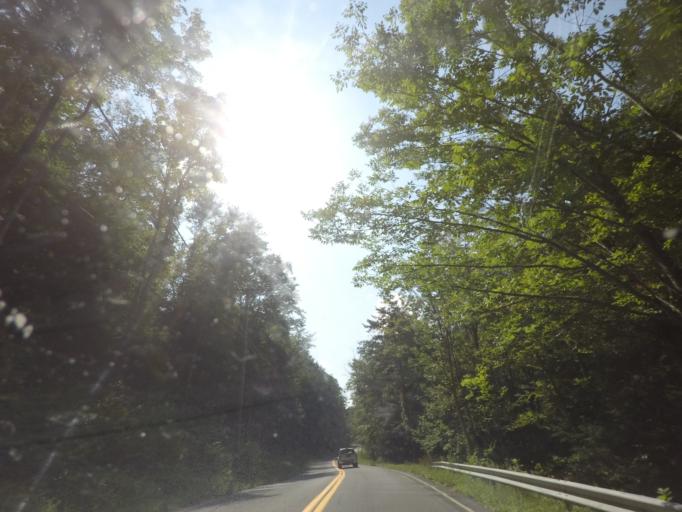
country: US
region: New York
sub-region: Rensselaer County
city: Poestenkill
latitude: 42.7087
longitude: -73.5098
